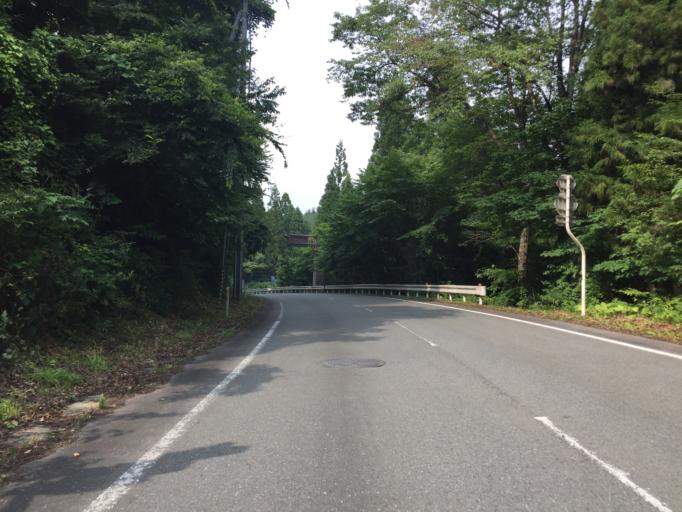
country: JP
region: Fukushima
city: Namie
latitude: 37.5539
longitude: 140.8744
